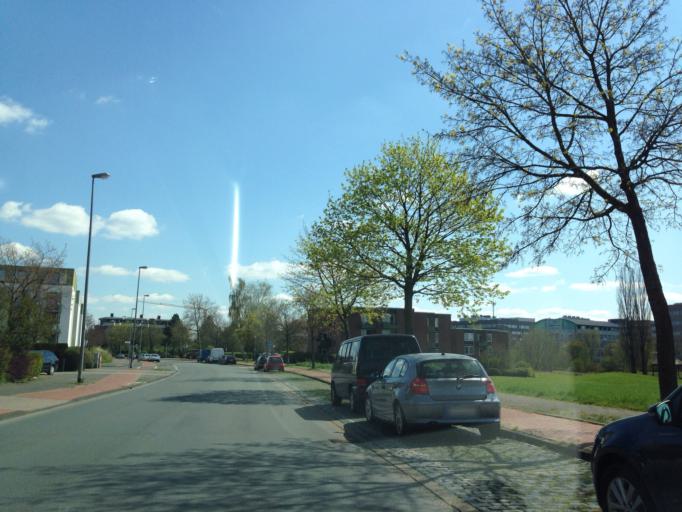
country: DE
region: North Rhine-Westphalia
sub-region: Regierungsbezirk Munster
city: Muenster
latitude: 51.9724
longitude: 7.5929
